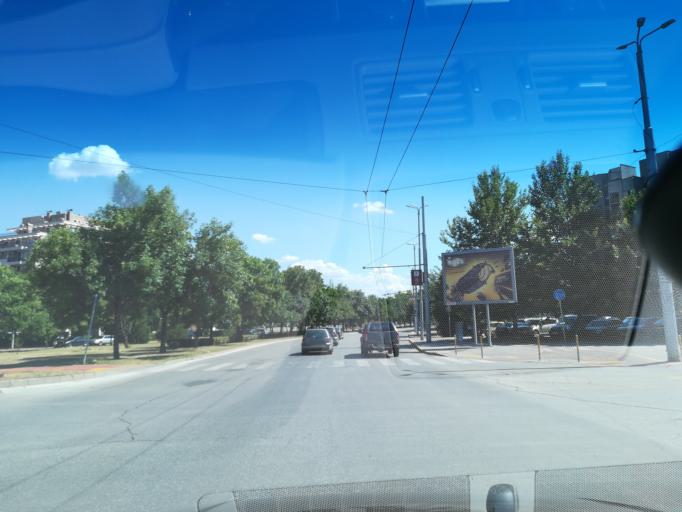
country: BG
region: Plovdiv
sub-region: Obshtina Plovdiv
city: Plovdiv
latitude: 42.1385
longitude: 24.7911
